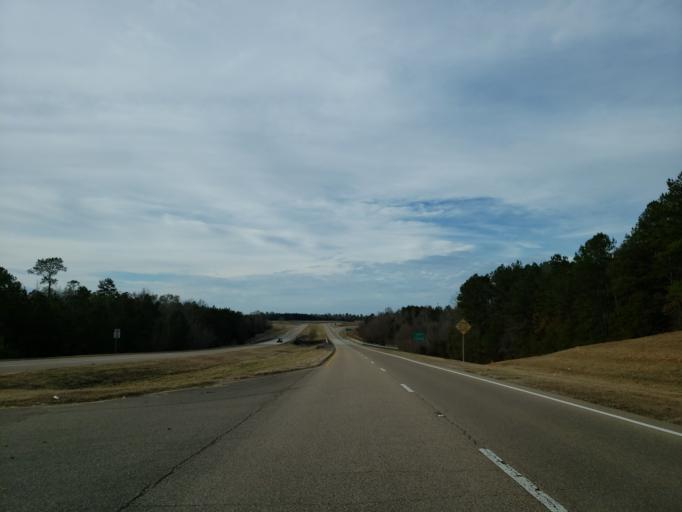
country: US
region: Mississippi
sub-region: Wayne County
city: Waynesboro
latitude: 31.6741
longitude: -88.6088
